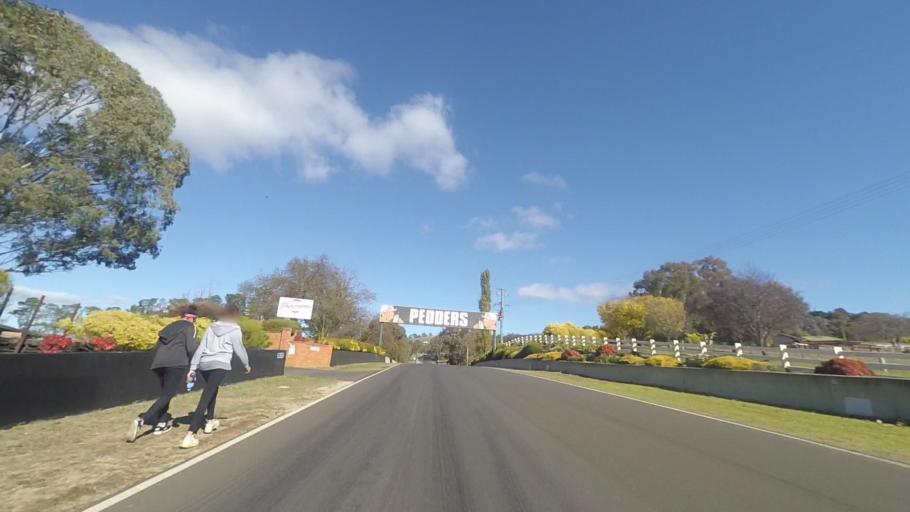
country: AU
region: New South Wales
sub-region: Bathurst Regional
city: Bathurst
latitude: -33.4448
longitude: 149.5545
